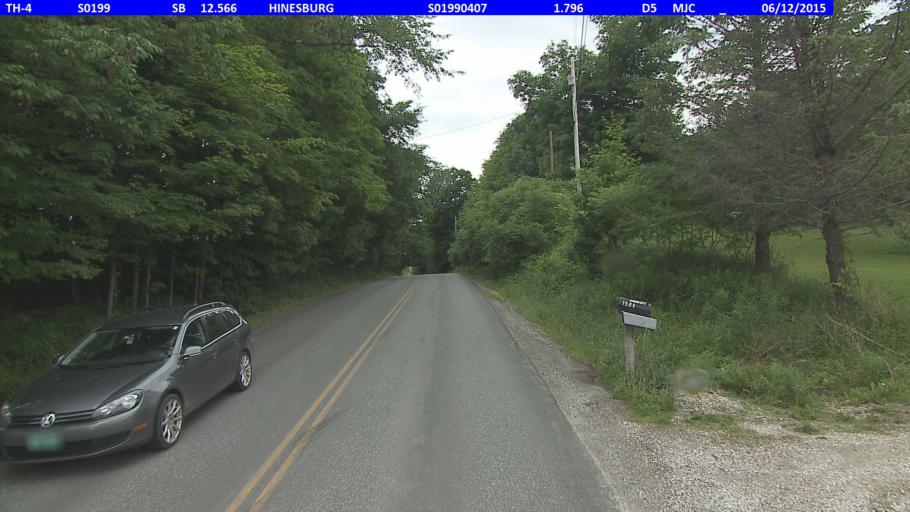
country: US
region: Vermont
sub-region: Chittenden County
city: Hinesburg
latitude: 44.3043
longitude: -73.1091
